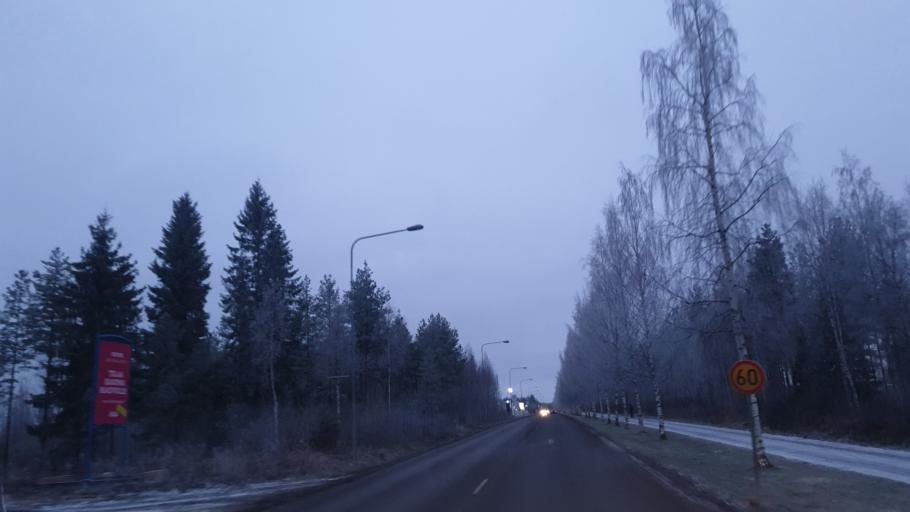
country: FI
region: Southern Ostrobothnia
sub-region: Seinaejoki
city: Nurmo
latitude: 62.7865
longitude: 22.9026
